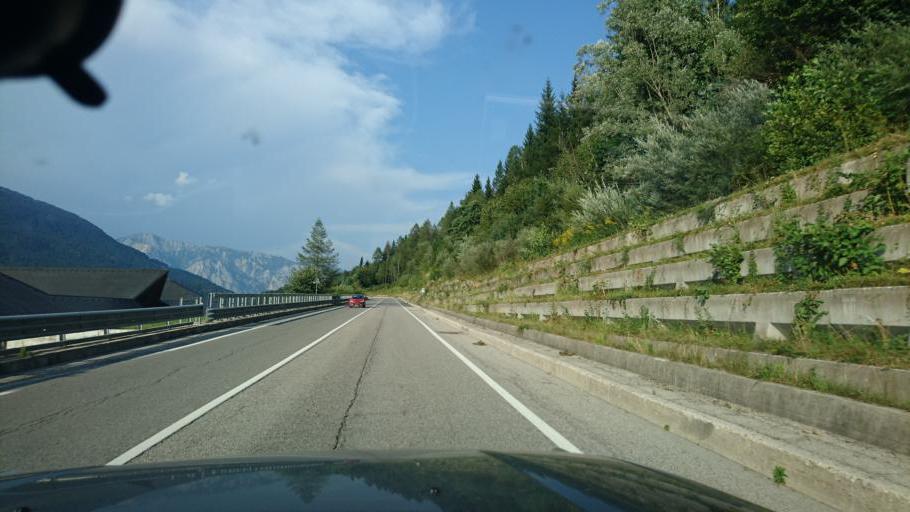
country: IT
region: Friuli Venezia Giulia
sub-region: Provincia di Udine
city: Tarvisio
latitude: 46.5053
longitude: 13.6072
